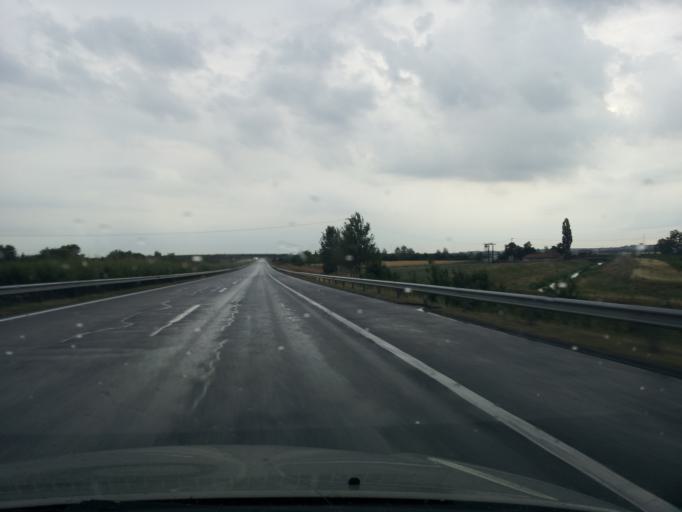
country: HU
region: Borsod-Abauj-Zemplen
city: Nyekladhaza
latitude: 47.9491
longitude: 20.8807
